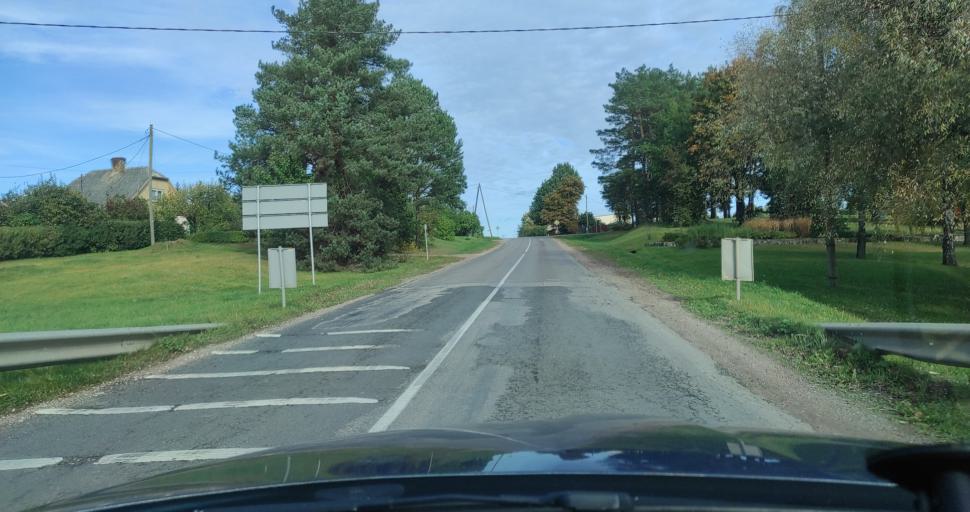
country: LV
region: Jaunpils
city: Jaunpils
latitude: 56.7319
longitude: 23.0130
